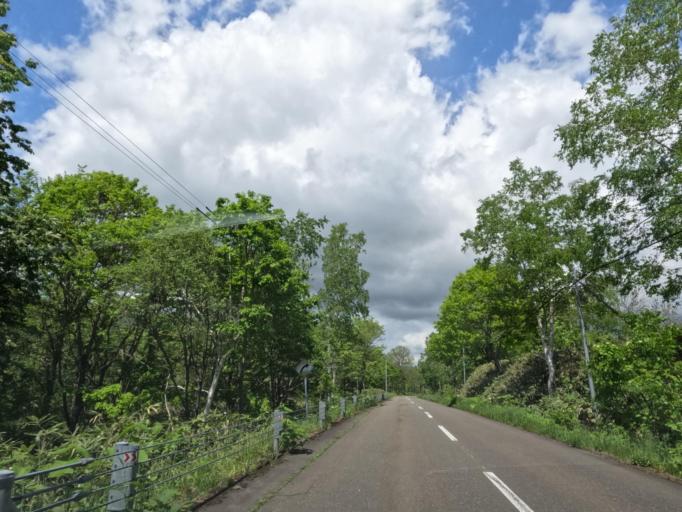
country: JP
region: Hokkaido
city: Tobetsu
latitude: 43.4336
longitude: 141.5801
